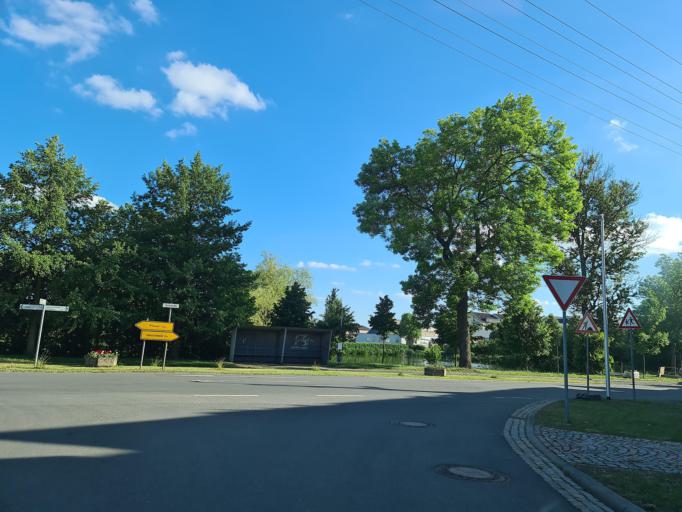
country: DE
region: Saxony
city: Plauen
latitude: 50.4934
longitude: 12.0903
